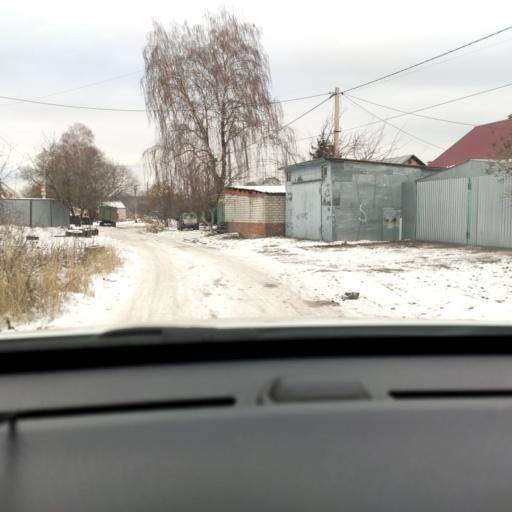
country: RU
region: Voronezj
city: Voronezh
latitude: 51.7052
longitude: 39.2646
